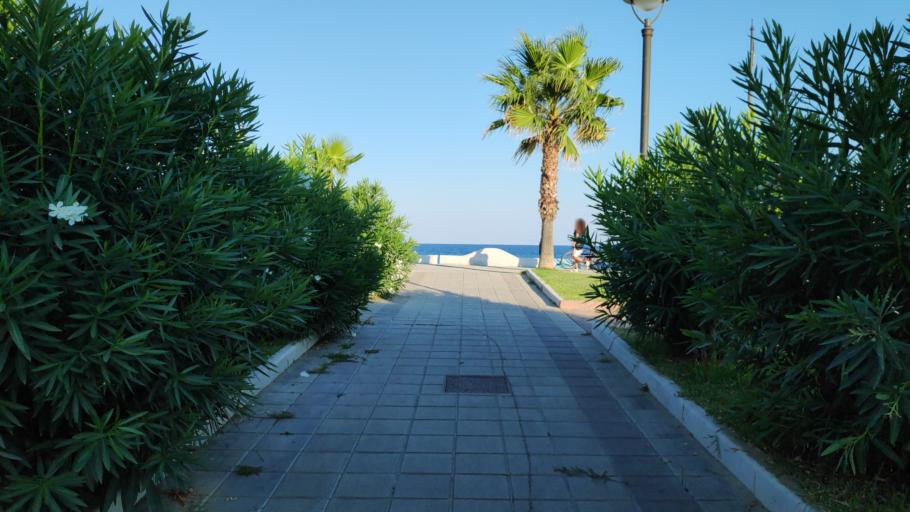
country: IT
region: Calabria
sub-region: Provincia di Reggio Calabria
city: Caulonia Marina
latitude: 38.3396
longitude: 16.4639
